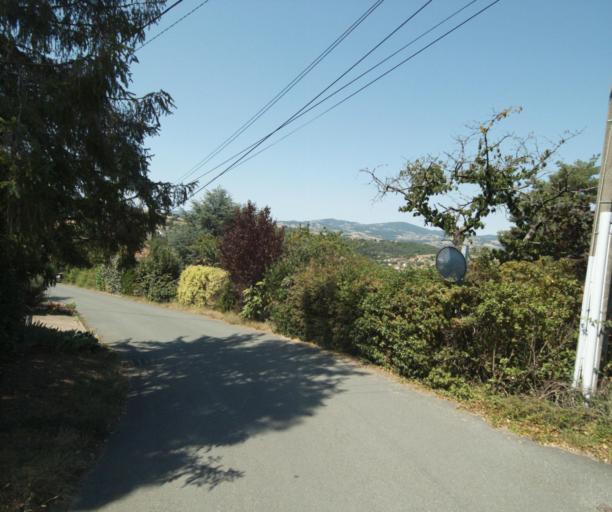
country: FR
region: Rhone-Alpes
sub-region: Departement du Rhone
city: Sourcieux-les-Mines
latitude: 45.7960
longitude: 4.6349
